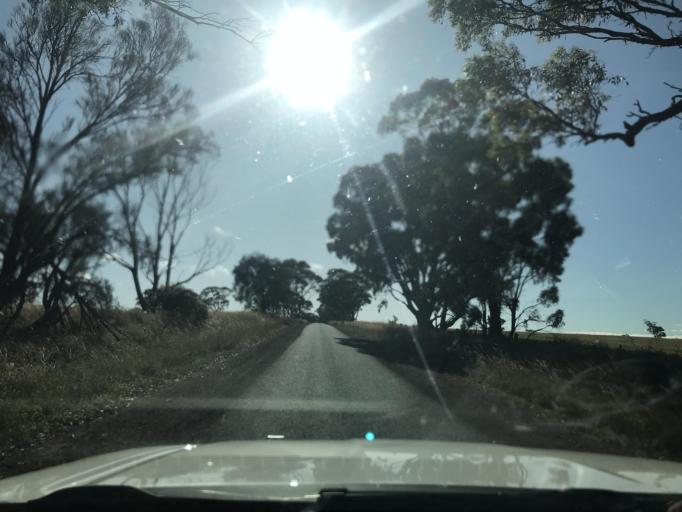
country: AU
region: Victoria
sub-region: Horsham
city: Horsham
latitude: -36.6980
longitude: 141.6036
